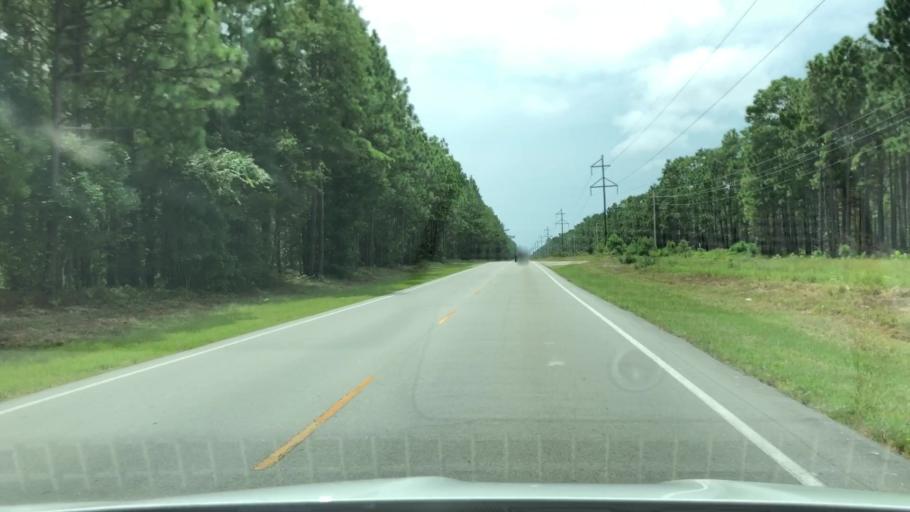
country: US
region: North Carolina
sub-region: Carteret County
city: Newport
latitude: 34.7680
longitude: -76.8667
